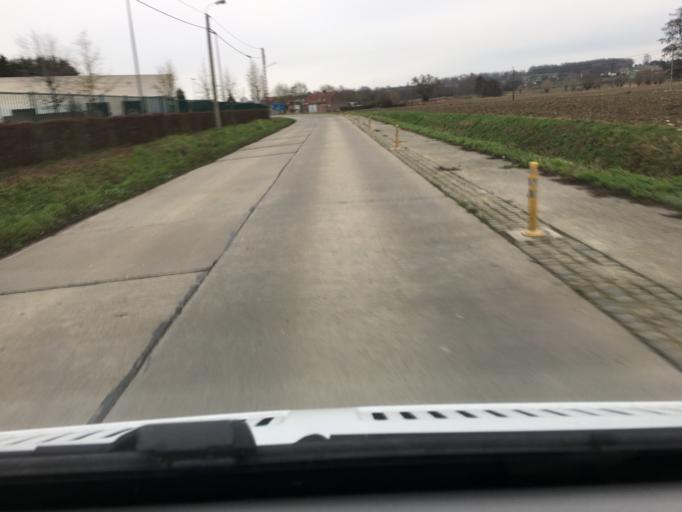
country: FR
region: Nord-Pas-de-Calais
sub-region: Departement du Nord
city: Bousbecque
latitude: 50.7819
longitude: 3.0892
